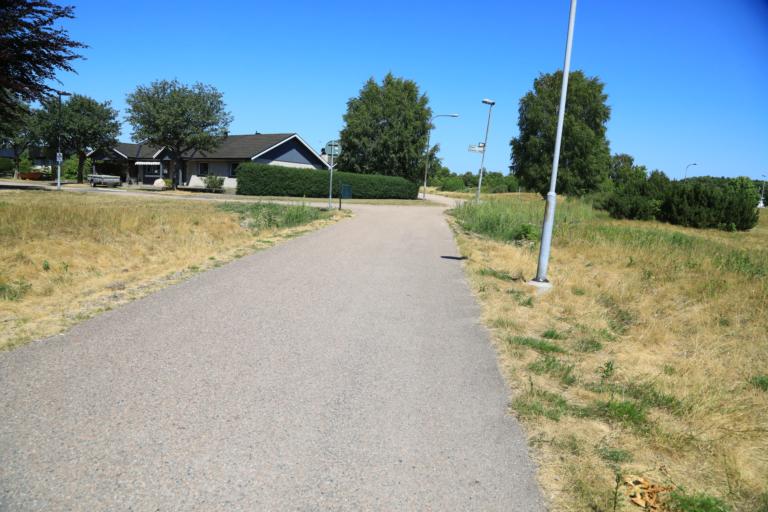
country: SE
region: Halland
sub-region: Halmstads Kommun
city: Fyllinge
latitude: 56.6638
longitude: 12.9113
